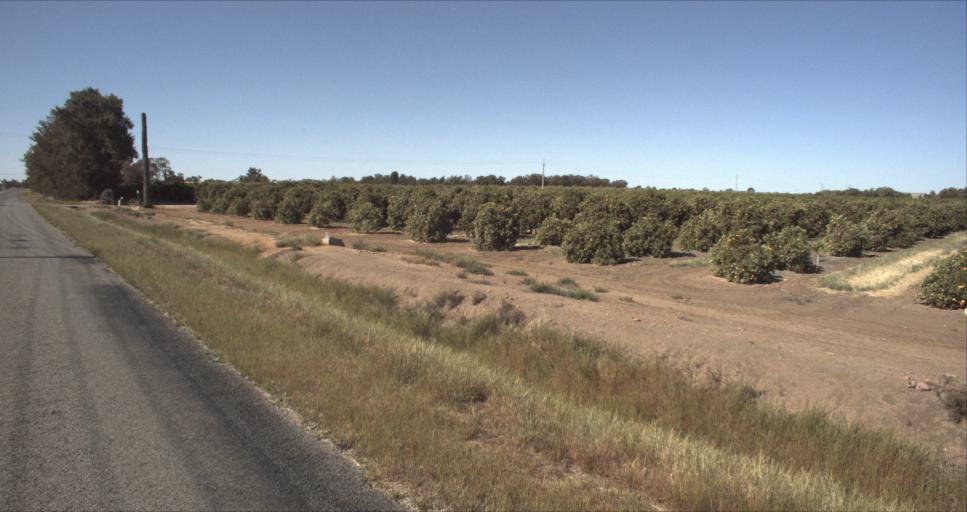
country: AU
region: New South Wales
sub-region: Leeton
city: Leeton
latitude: -34.5676
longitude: 146.3823
